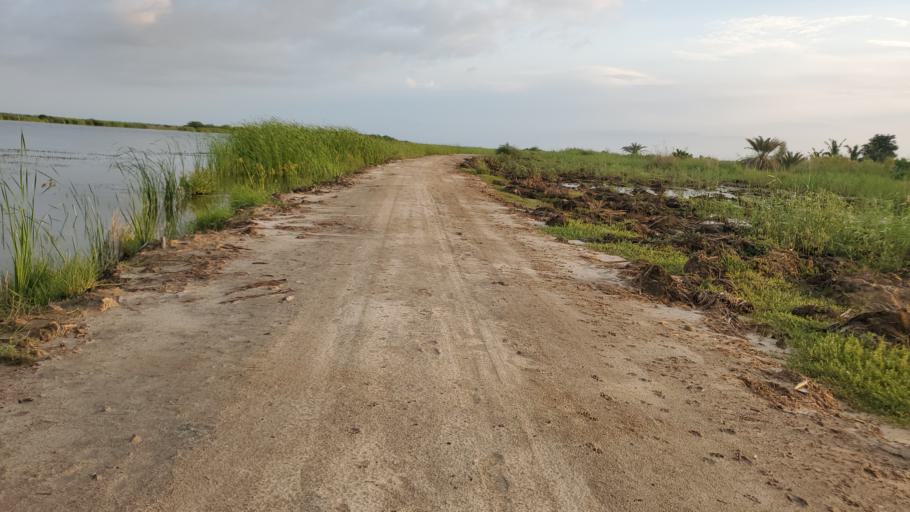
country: SN
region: Saint-Louis
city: Saint-Louis
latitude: 16.0141
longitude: -16.4005
